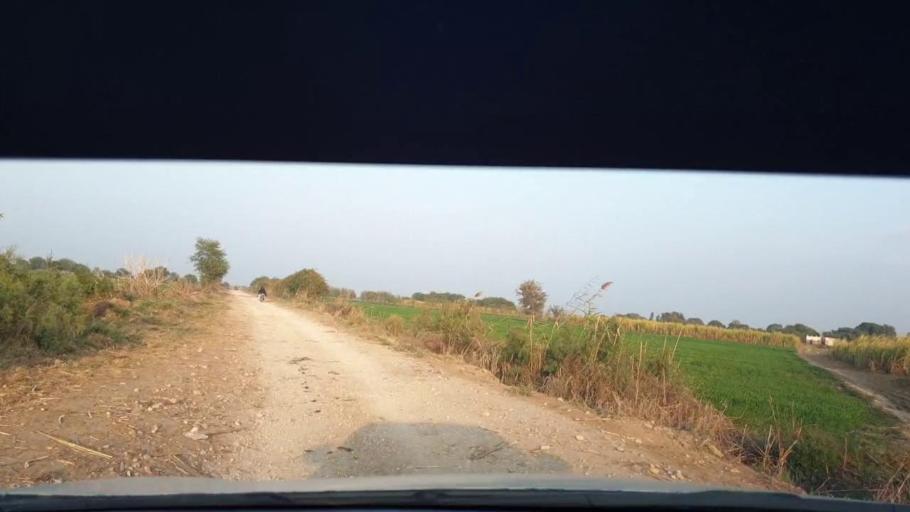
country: PK
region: Sindh
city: Berani
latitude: 25.7401
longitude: 68.9671
